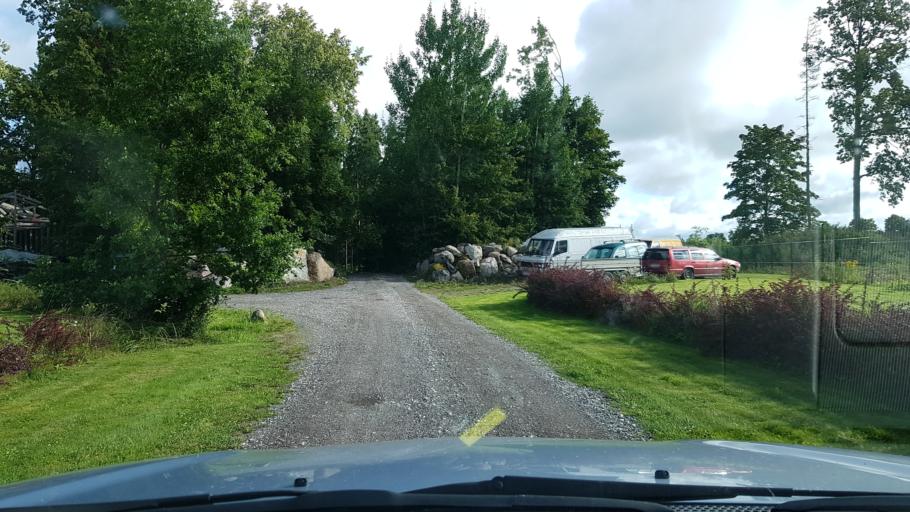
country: EE
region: Harju
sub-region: Rae vald
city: Vaida
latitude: 59.2686
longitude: 25.0229
